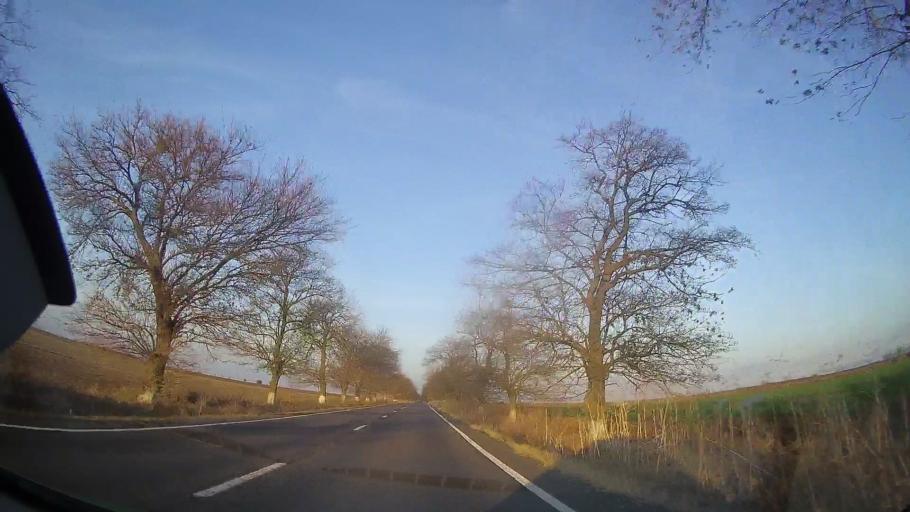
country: RO
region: Constanta
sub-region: Comuna Amzacea
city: Amzacea
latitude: 43.9492
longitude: 28.3806
